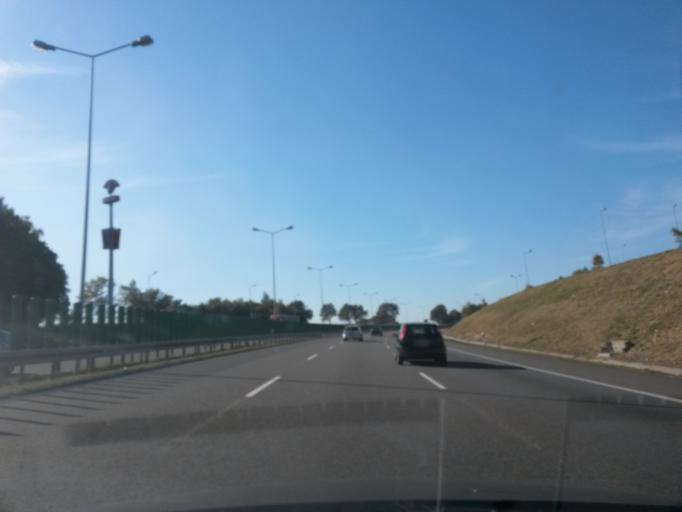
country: PL
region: Opole Voivodeship
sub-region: Powiat strzelecki
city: Lesnica
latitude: 50.4621
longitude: 18.1604
